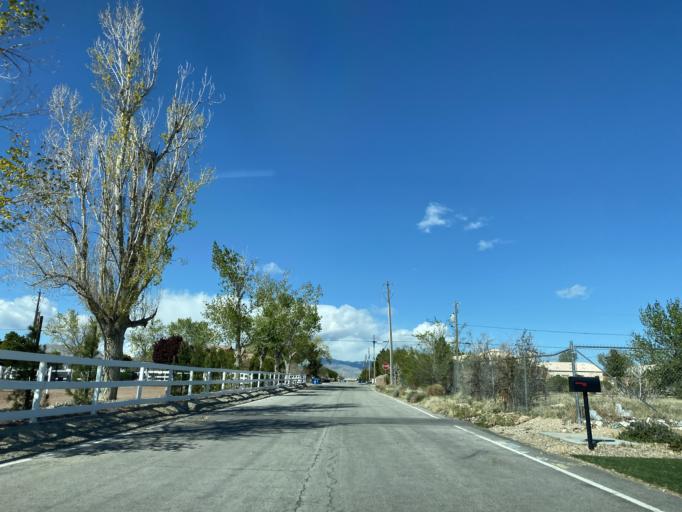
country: US
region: Nevada
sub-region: Clark County
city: North Las Vegas
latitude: 36.3319
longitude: -115.2820
